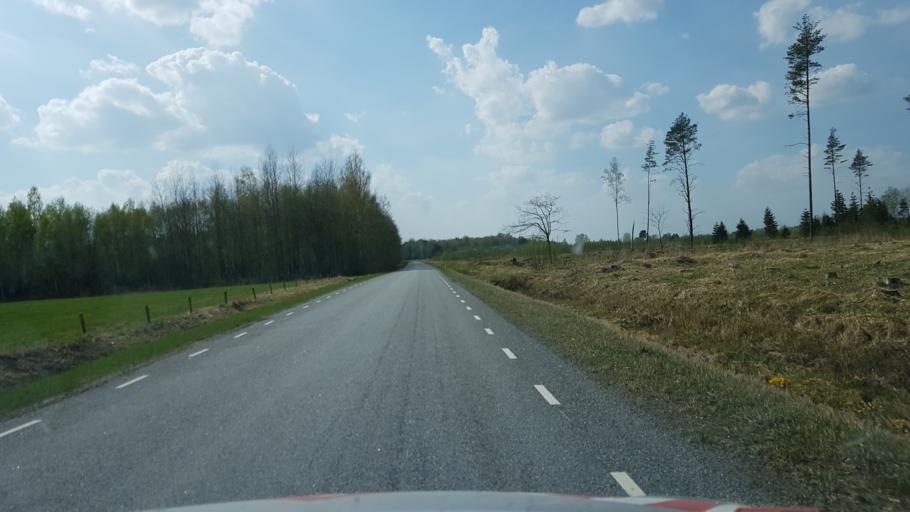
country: EE
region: Paernumaa
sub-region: Sauga vald
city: Sauga
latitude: 58.4400
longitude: 24.5701
